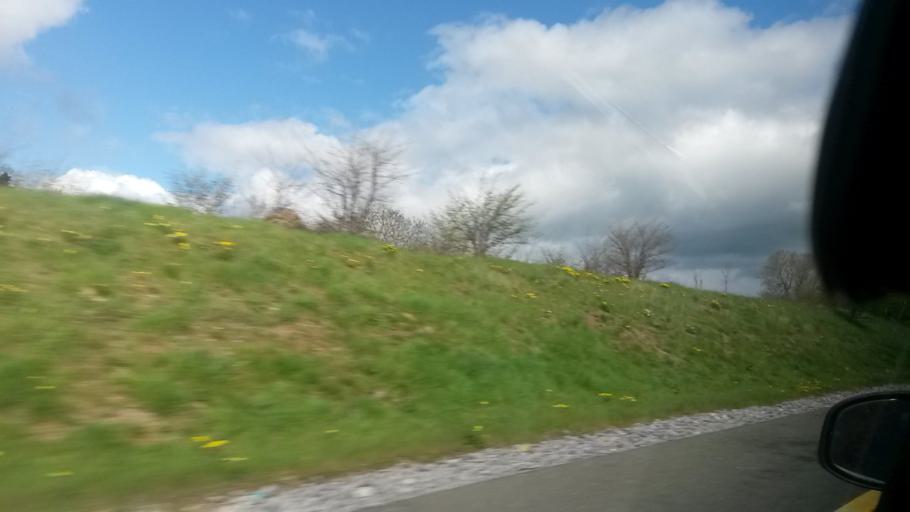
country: IE
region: Munster
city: Cahir
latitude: 52.4276
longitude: -7.9148
